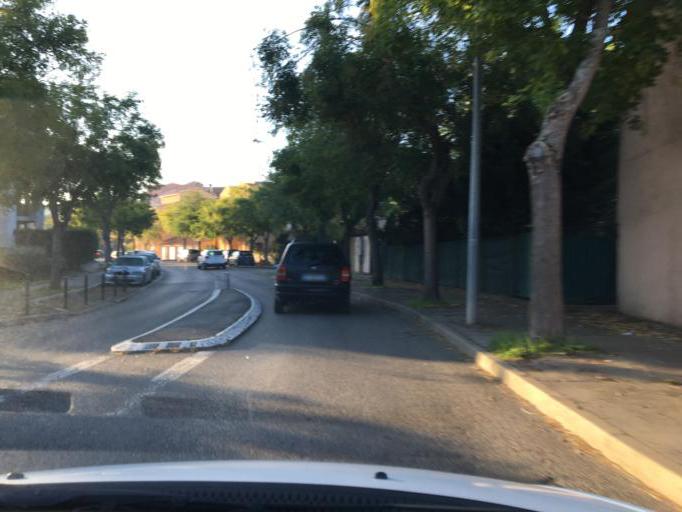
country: FR
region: Provence-Alpes-Cote d'Azur
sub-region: Departement des Bouches-du-Rhone
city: Aix-en-Provence
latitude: 43.5291
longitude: 5.4104
